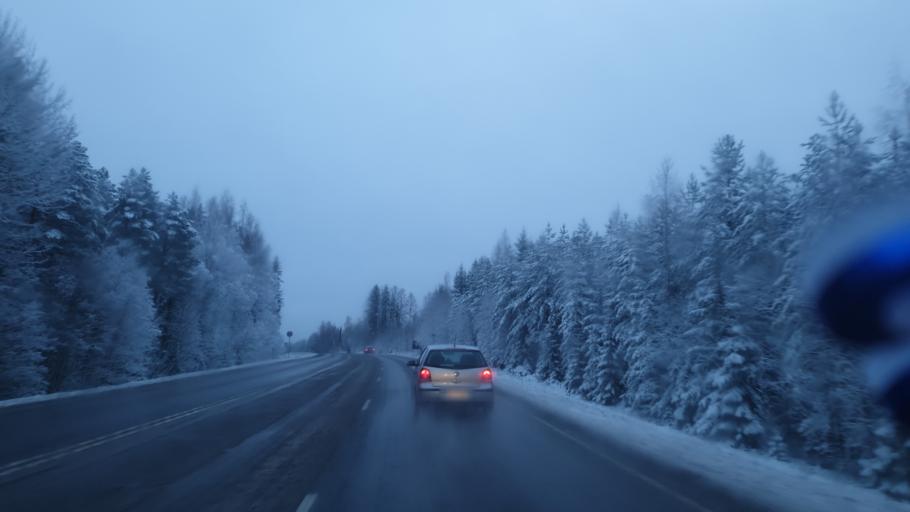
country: FI
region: Central Finland
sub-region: Saarijaervi-Viitasaari
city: Viitasaari
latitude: 63.0350
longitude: 25.8099
